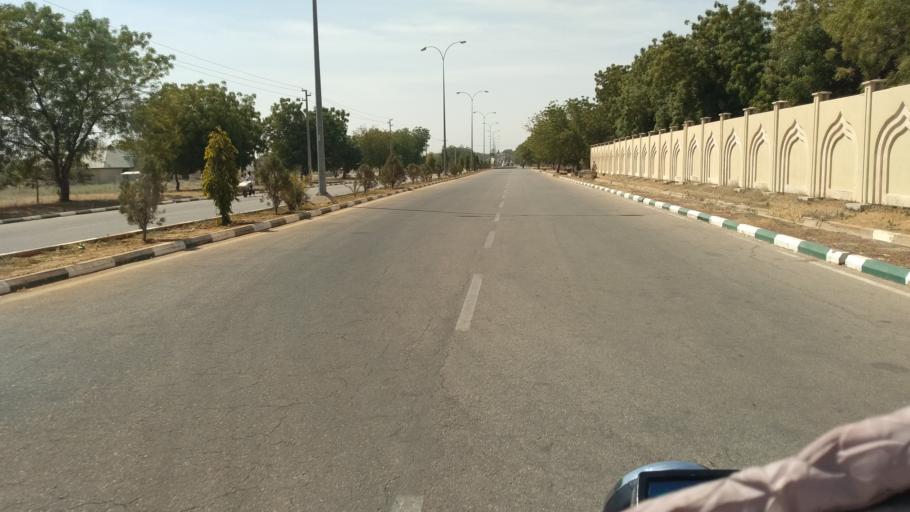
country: NG
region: Jigawa
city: Dutse
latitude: 11.6843
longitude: 9.3353
